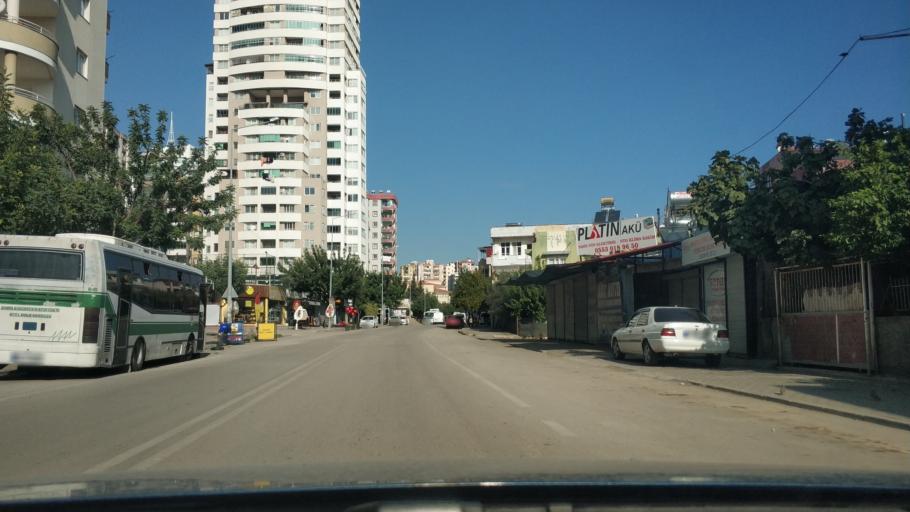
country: TR
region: Adana
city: Seyhan
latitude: 37.0197
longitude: 35.2913
